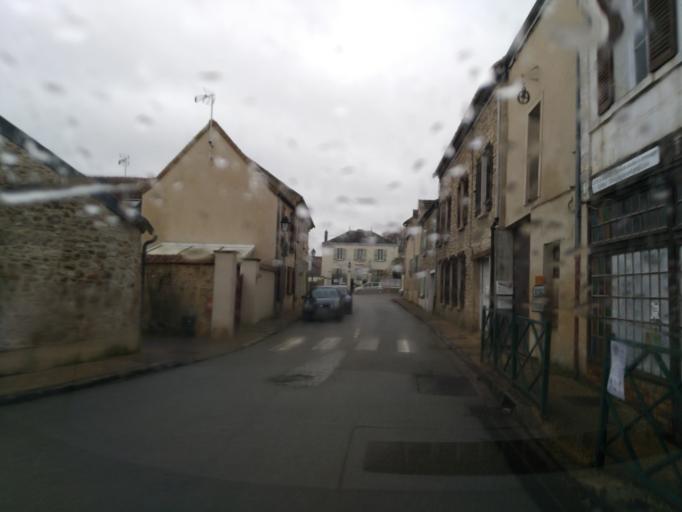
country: FR
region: Ile-de-France
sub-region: Departement des Yvelines
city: Thoiry
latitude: 48.8604
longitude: 1.8184
